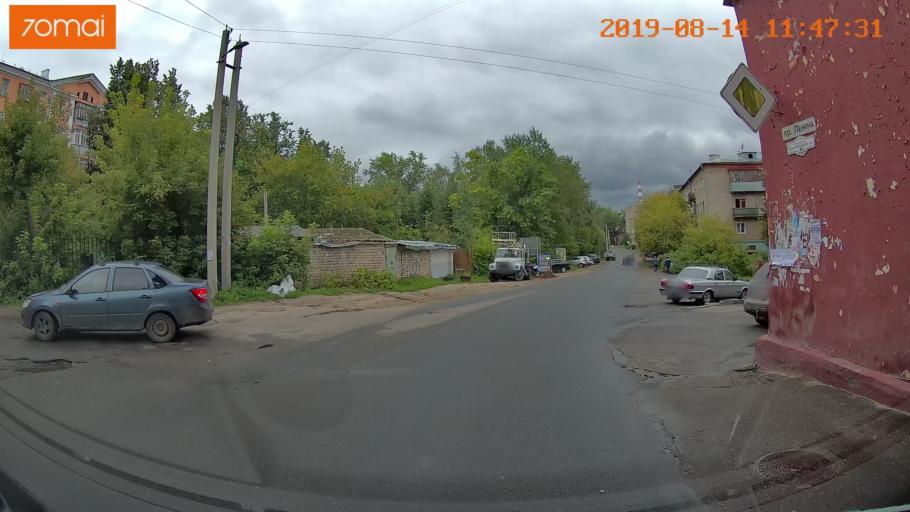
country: RU
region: Ivanovo
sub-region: Gorod Ivanovo
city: Ivanovo
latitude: 57.0141
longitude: 40.9691
